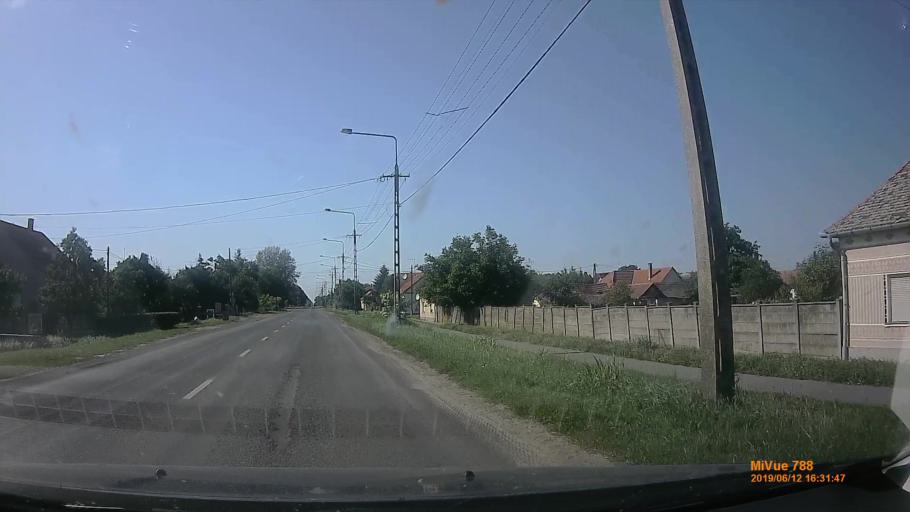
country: HU
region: Csongrad
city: Apatfalva
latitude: 46.1783
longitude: 20.5739
